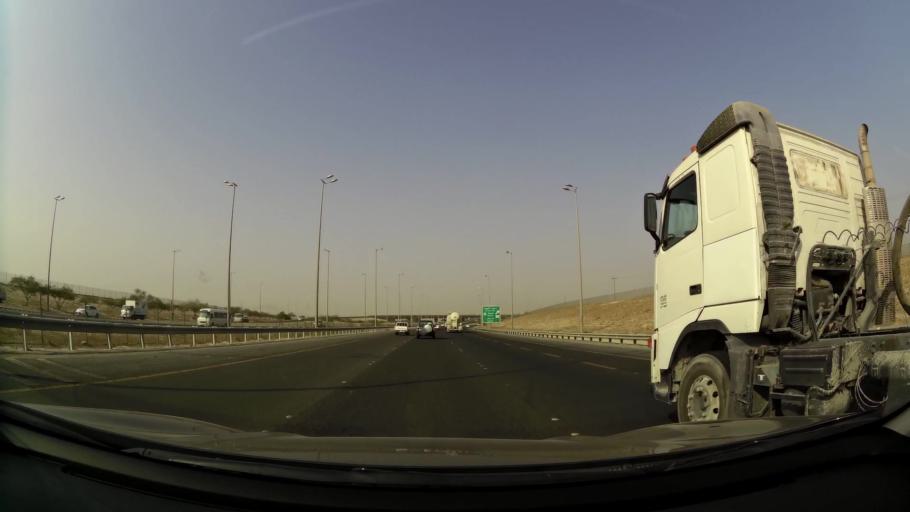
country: KW
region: Mubarak al Kabir
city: Mubarak al Kabir
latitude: 29.1794
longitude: 48.0017
